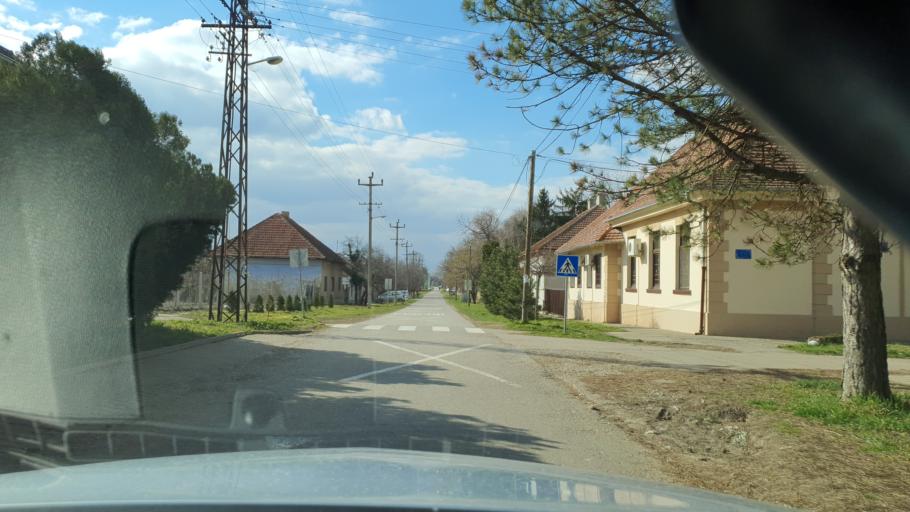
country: RS
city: Kulpin
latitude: 45.4009
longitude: 19.5883
